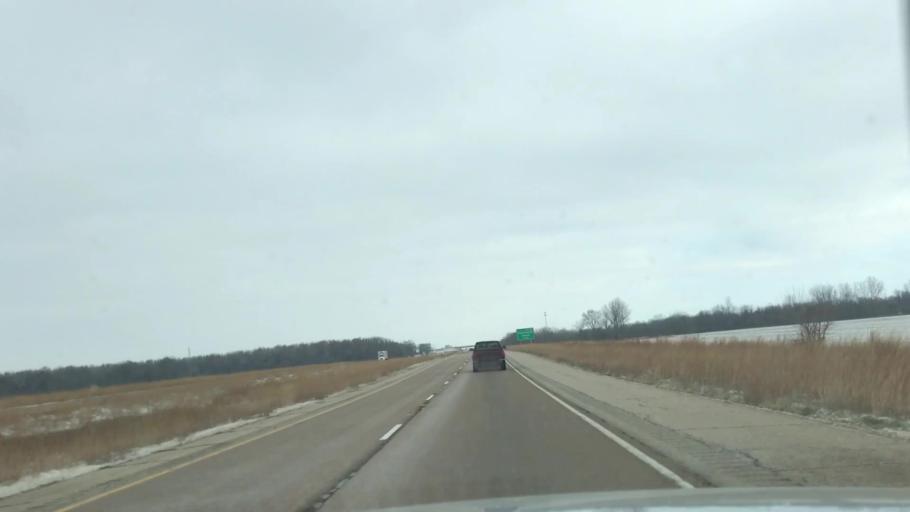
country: US
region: Illinois
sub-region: Montgomery County
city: Raymond
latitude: 39.4291
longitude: -89.6434
